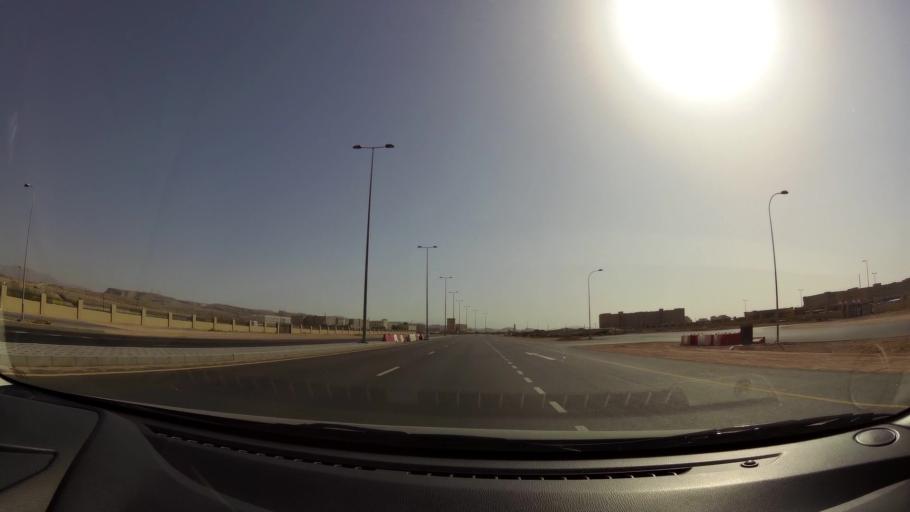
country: OM
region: Muhafazat Masqat
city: Bawshar
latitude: 23.5747
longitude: 58.2888
